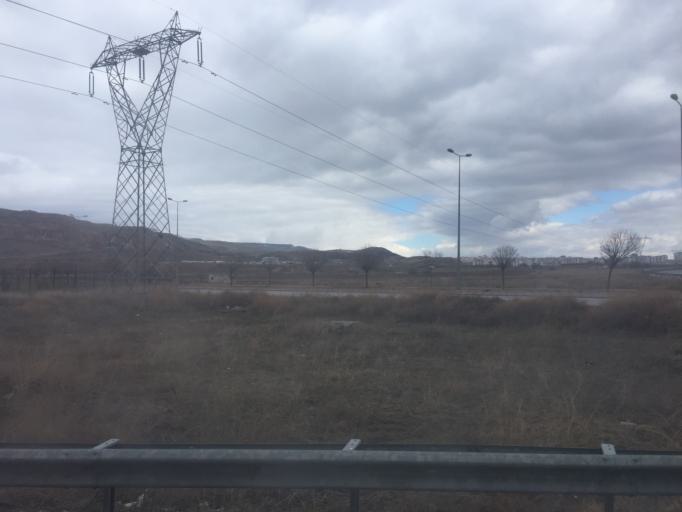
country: TR
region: Kayseri
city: Erkilet
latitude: 38.7839
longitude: 35.4115
